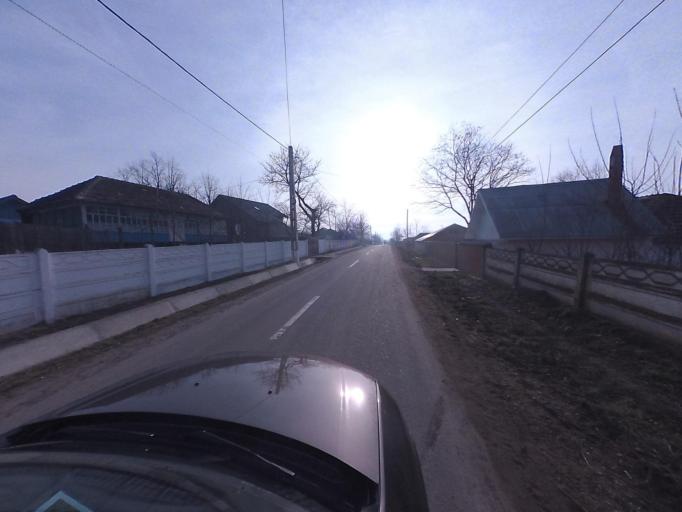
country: RO
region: Vaslui
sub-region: Comuna Solesti
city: Solesti
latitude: 46.8096
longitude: 27.7756
